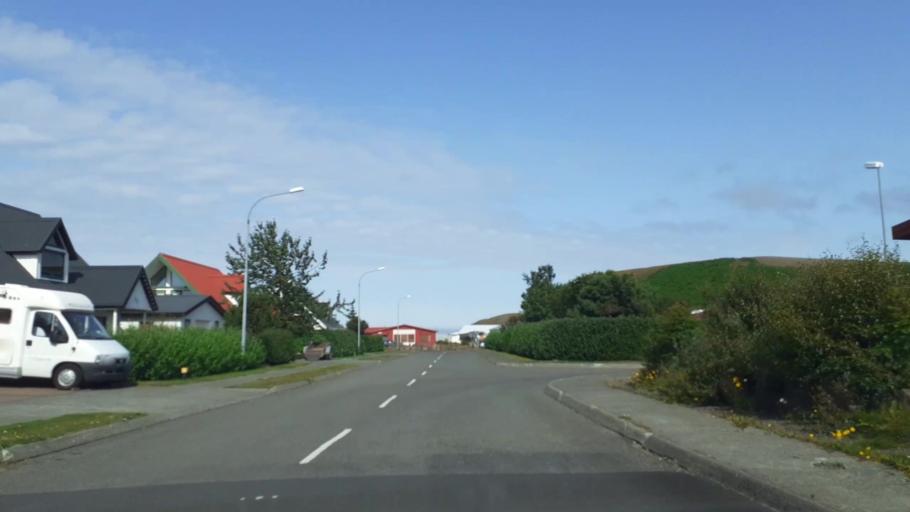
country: IS
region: Northwest
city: Saudarkrokur
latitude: 65.6639
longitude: -20.2901
